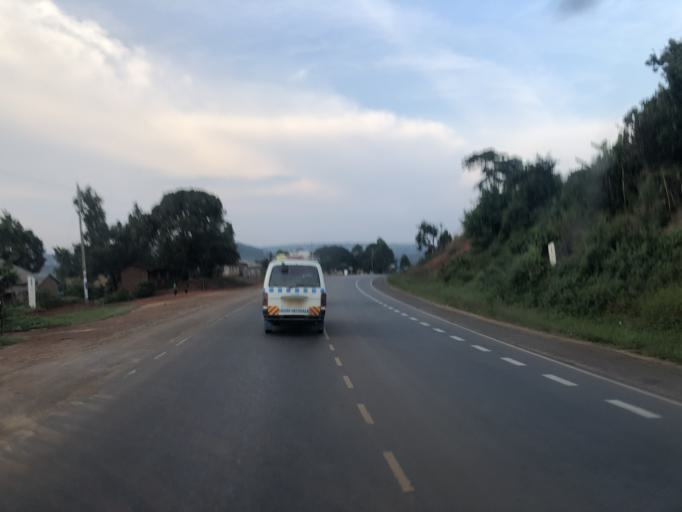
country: UG
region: Central Region
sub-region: Mpigi District
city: Mpigi
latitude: 0.2391
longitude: 32.3490
